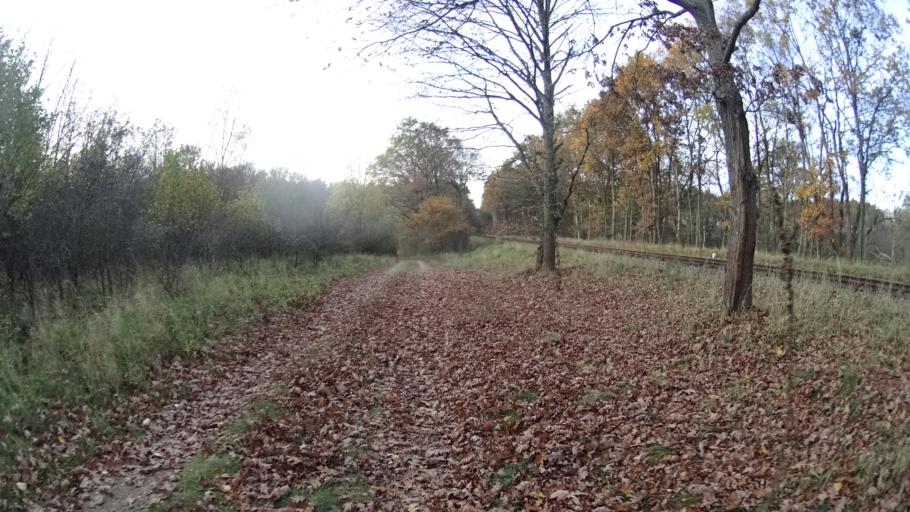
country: DE
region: Lower Saxony
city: Deutsch Evern
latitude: 53.2196
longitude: 10.4439
